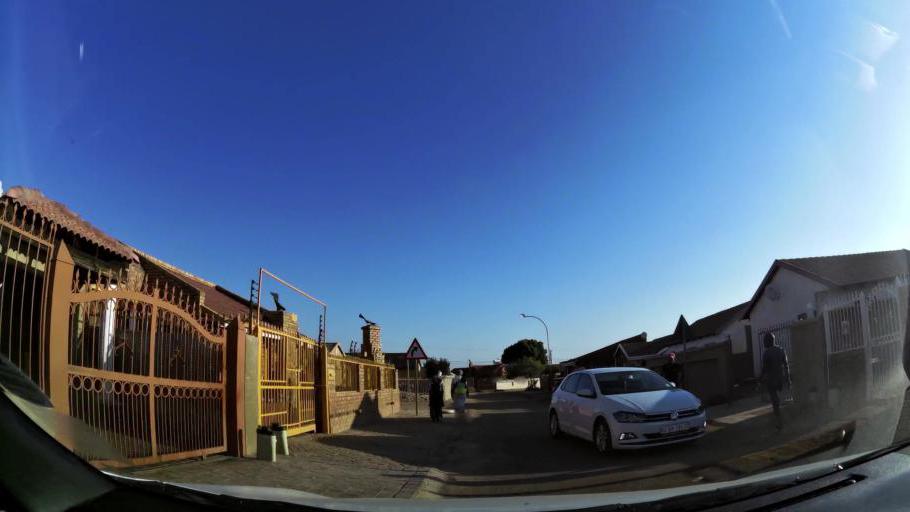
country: ZA
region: Gauteng
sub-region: City of Tshwane Metropolitan Municipality
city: Cullinan
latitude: -25.7284
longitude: 28.3994
